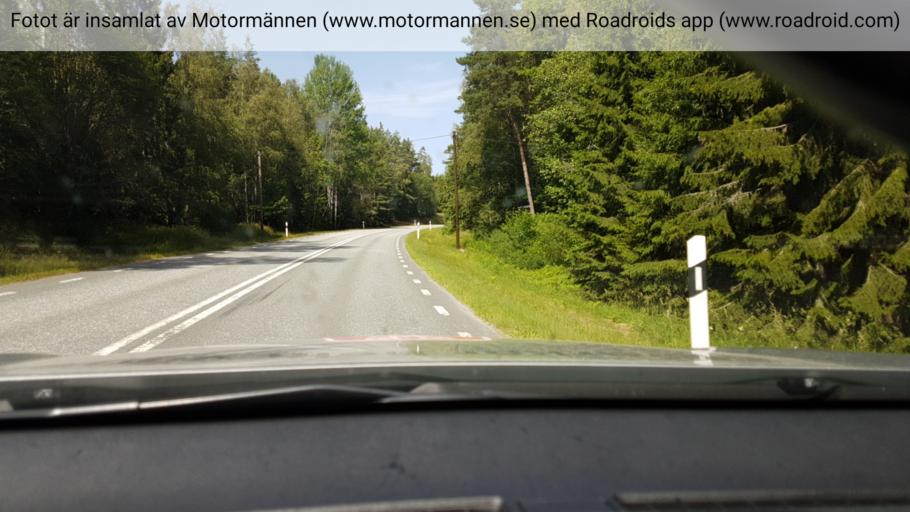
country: SE
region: Joenkoeping
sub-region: Nassjo Kommun
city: Bodafors
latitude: 57.5454
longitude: 14.7897
